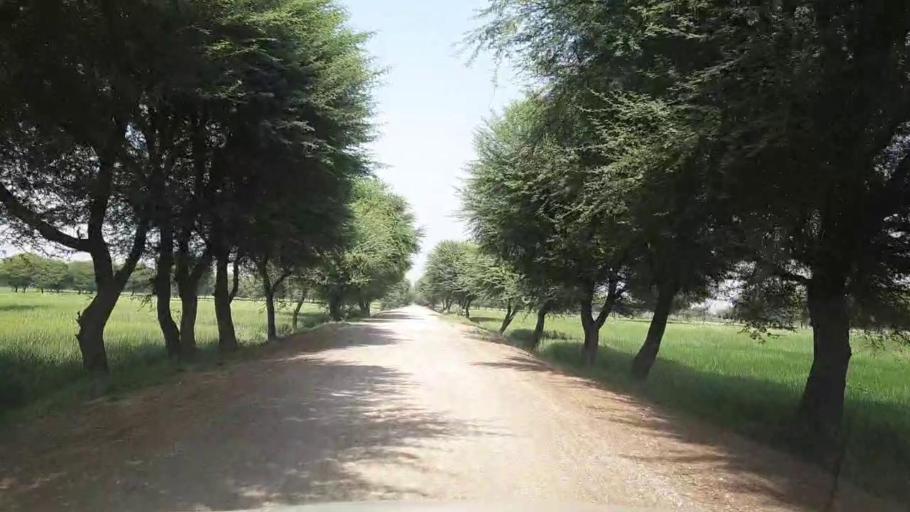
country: PK
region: Sindh
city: Dhoro Naro
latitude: 25.4790
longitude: 69.6199
